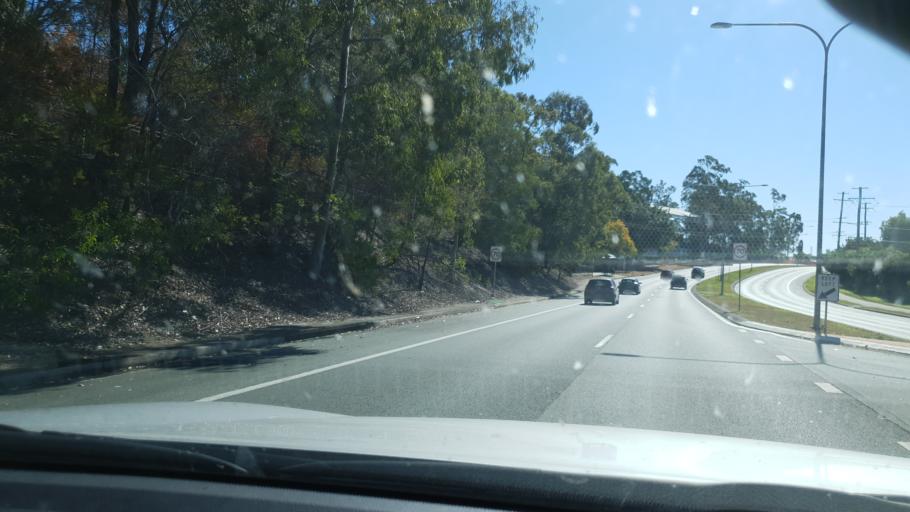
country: AU
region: Queensland
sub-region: Brisbane
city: Bridegman Downs
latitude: -27.3538
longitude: 152.9682
